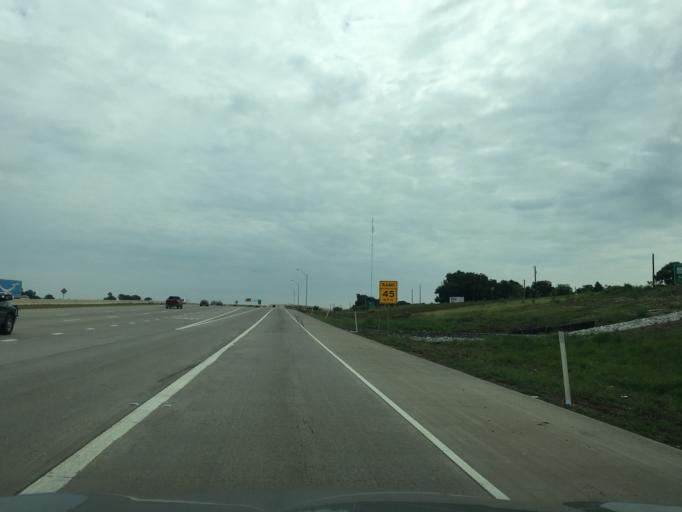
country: US
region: Texas
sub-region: Collin County
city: Melissa
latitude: 33.2603
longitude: -96.6050
